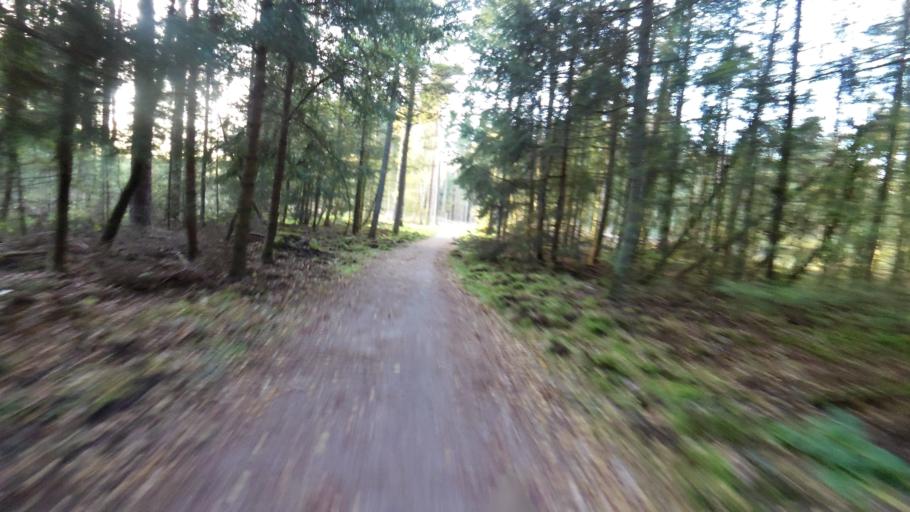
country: NL
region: Gelderland
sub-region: Gemeente Epe
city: Epe
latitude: 52.3741
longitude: 5.9582
